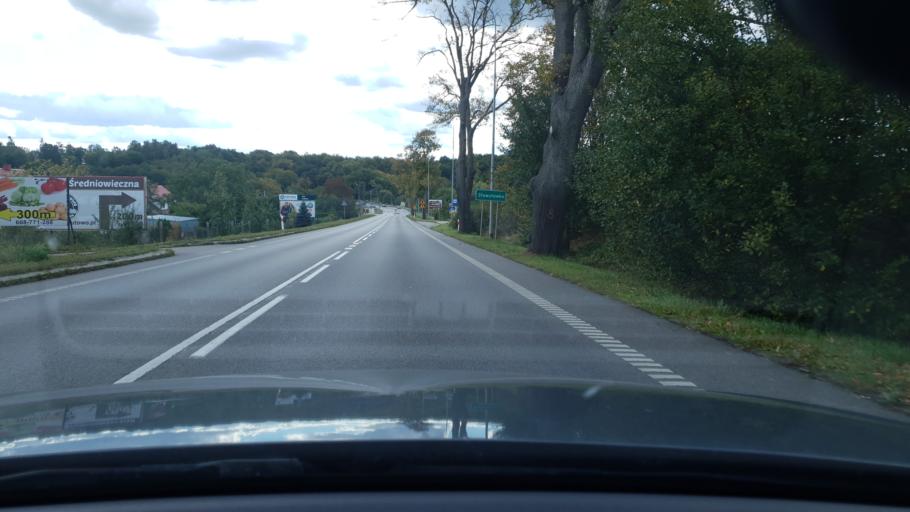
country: PL
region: Pomeranian Voivodeship
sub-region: Powiat wejherowski
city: Rekowo Dolne
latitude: 54.6646
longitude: 18.3655
